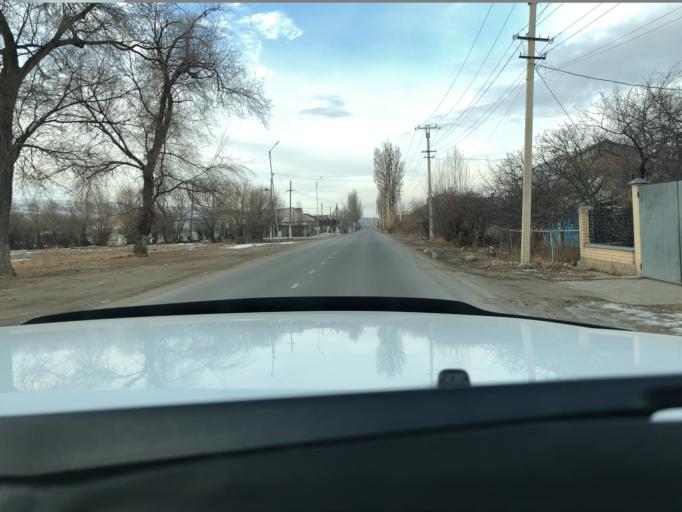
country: KG
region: Ysyk-Koel
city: Karakol
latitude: 42.4697
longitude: 78.3792
